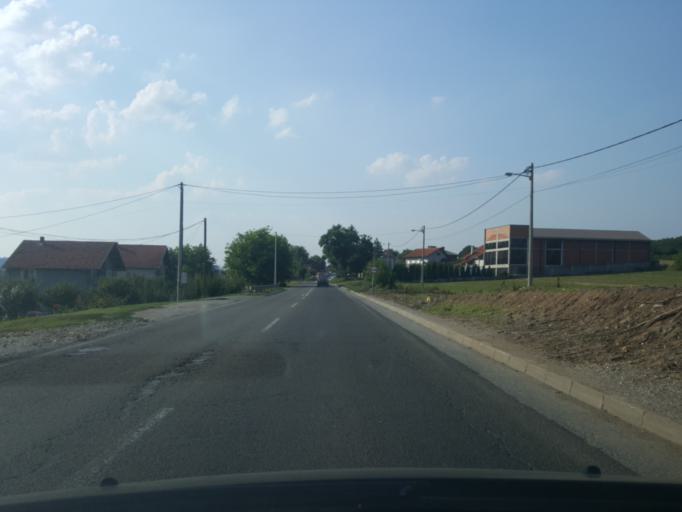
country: RS
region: Central Serbia
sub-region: Belgrade
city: Mladenovac
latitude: 44.4663
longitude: 20.6675
